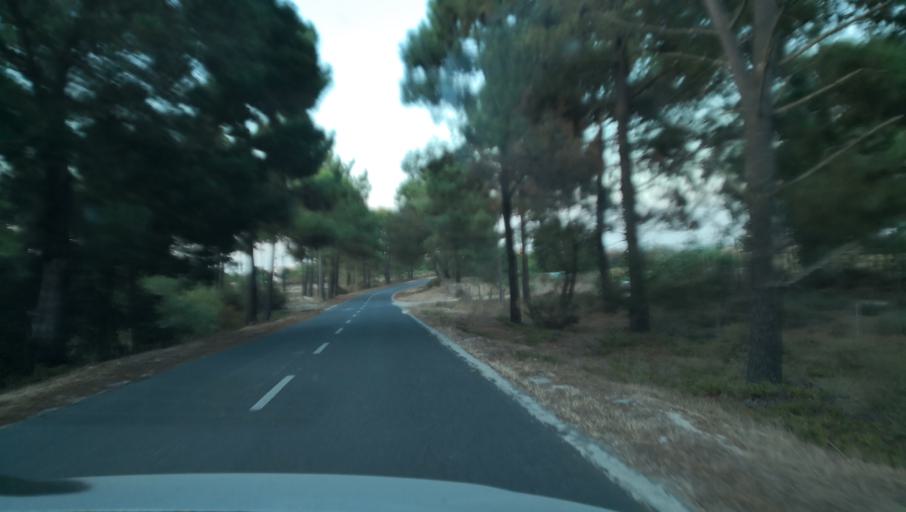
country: PT
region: Setubal
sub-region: Setubal
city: Setubal
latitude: 38.3913
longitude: -8.7798
